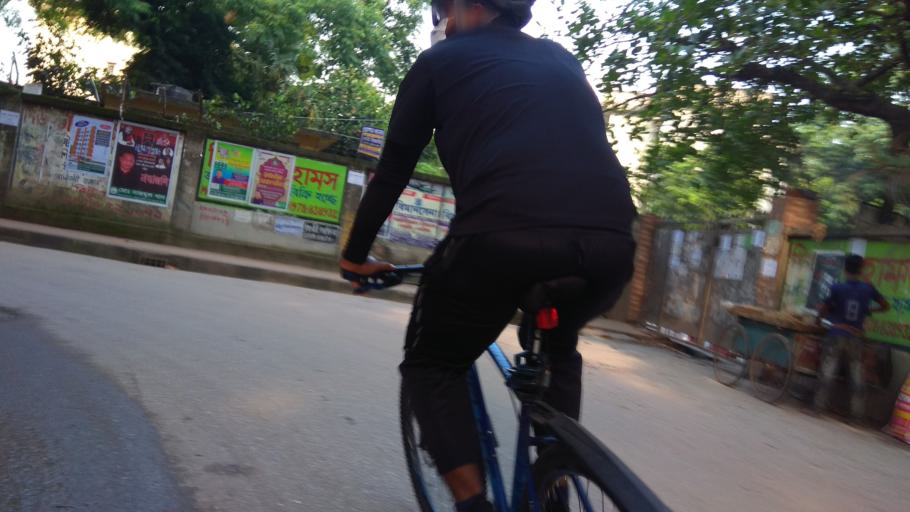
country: BD
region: Dhaka
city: Tungi
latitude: 23.8249
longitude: 90.3944
